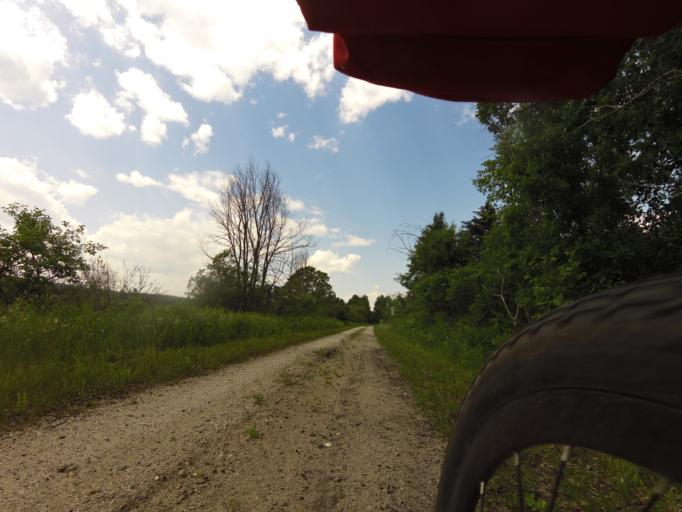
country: CA
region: Quebec
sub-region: Outaouais
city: Maniwaki
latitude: 46.0552
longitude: -76.1048
